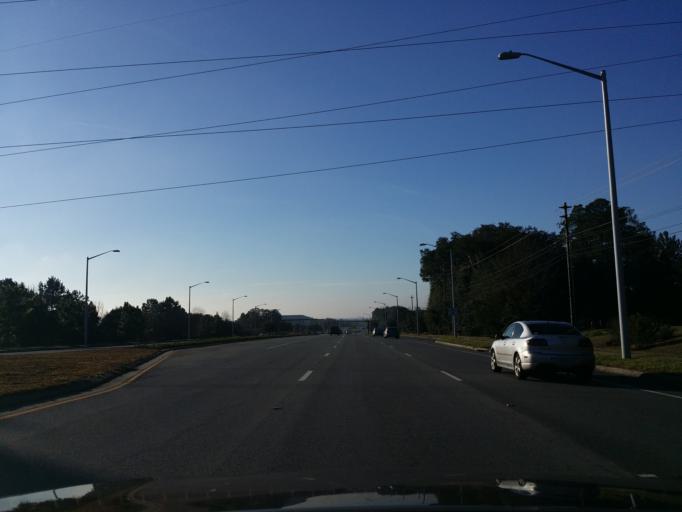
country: US
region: Florida
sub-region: Leon County
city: Tallahassee
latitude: 30.4054
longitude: -84.2352
